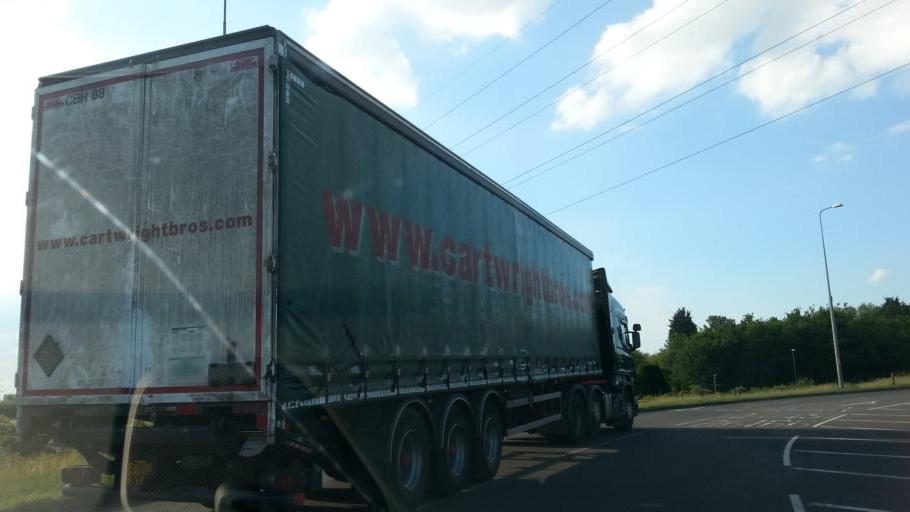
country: GB
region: England
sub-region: Nottinghamshire
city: Farndon
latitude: 53.0640
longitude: -0.8366
